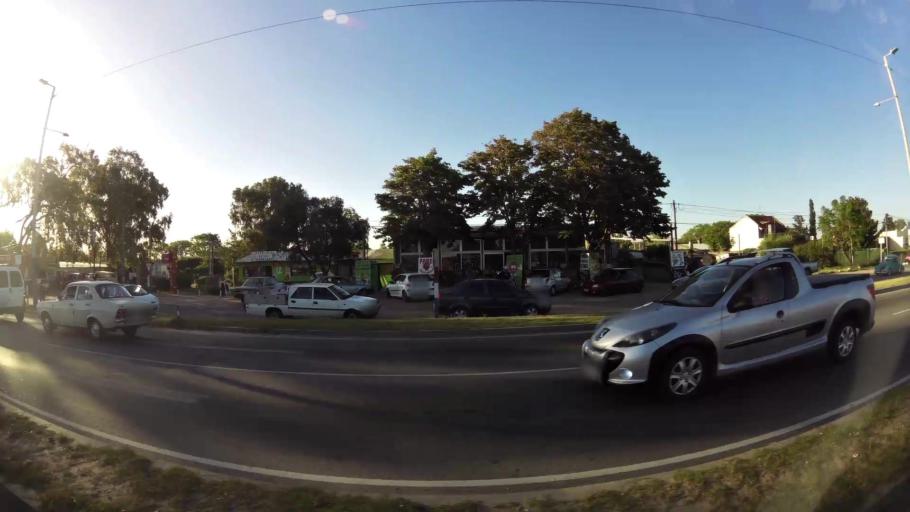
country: UY
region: Canelones
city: Paso de Carrasco
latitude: -34.8606
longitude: -56.0517
